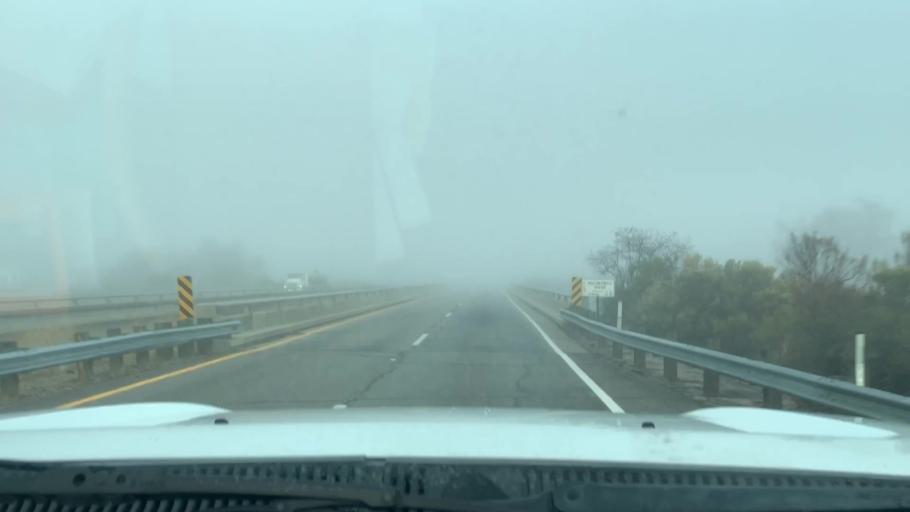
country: US
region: California
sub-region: San Luis Obispo County
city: San Miguel
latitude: 35.8192
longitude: -120.7567
